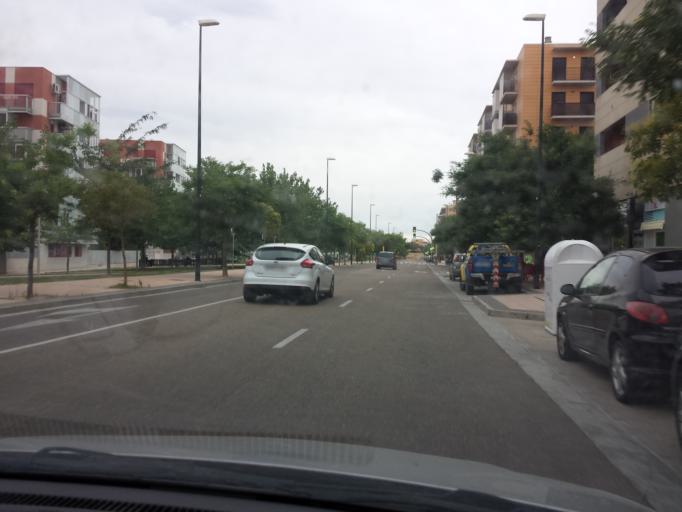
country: ES
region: Aragon
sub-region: Provincia de Zaragoza
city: Montecanal
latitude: 41.6217
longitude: -0.9306
